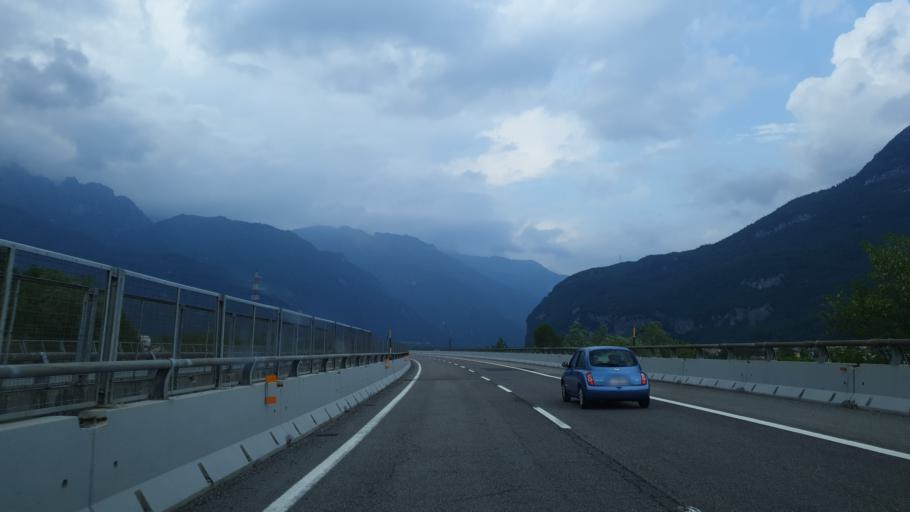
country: IT
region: Veneto
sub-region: Provincia di Belluno
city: Soccher-Paiane-Casan-Arsie
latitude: 46.1701
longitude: 12.3100
